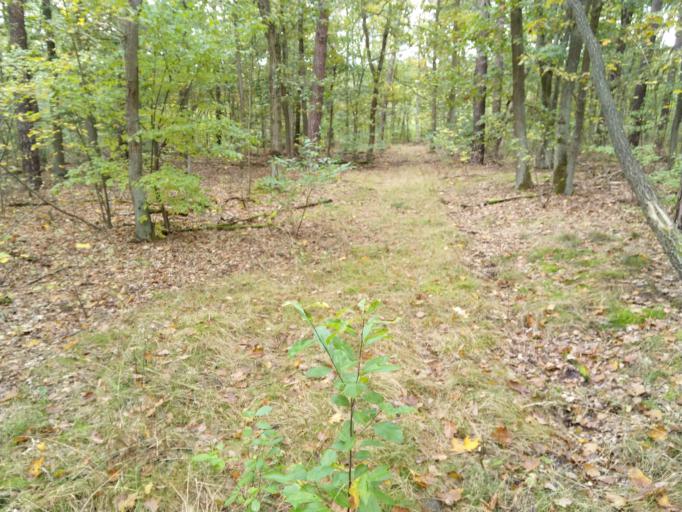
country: DE
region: Berlin
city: Rahnsdorf
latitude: 52.4533
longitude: 13.6605
